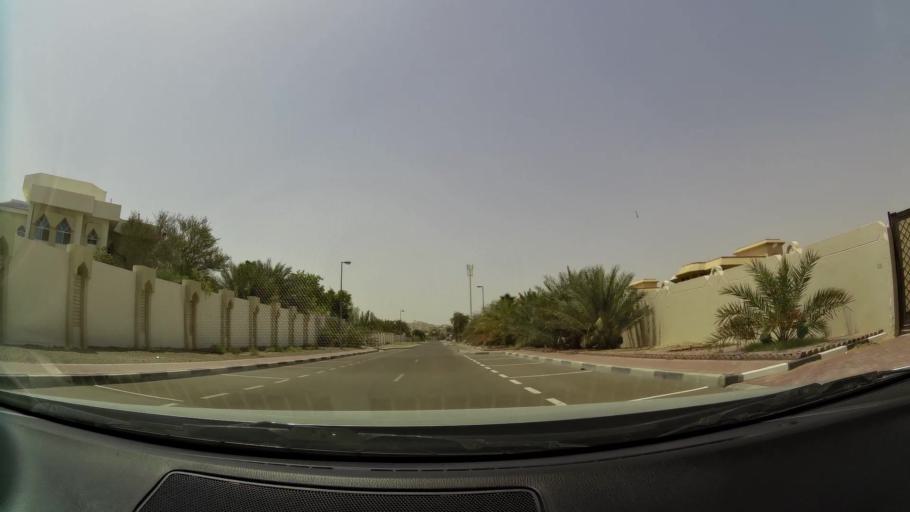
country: AE
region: Abu Dhabi
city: Al Ain
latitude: 24.1855
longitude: 55.7257
